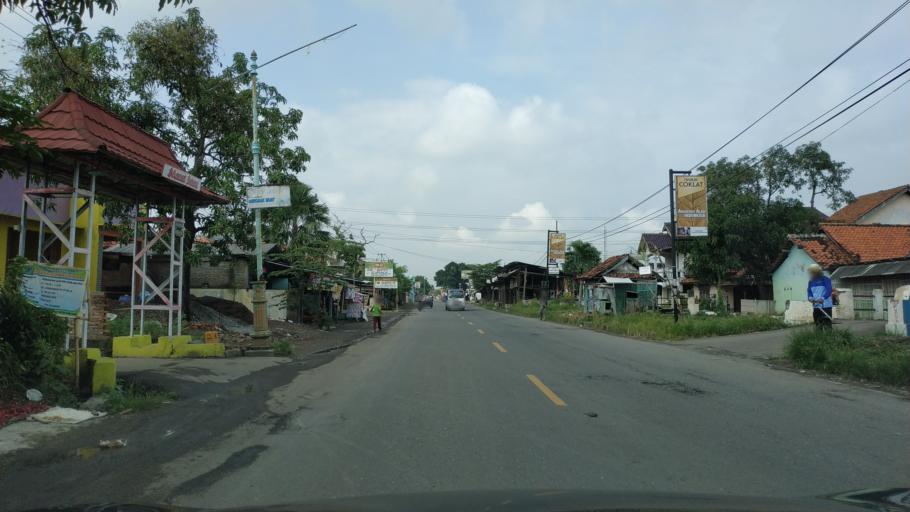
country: ID
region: Central Java
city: Ketanggungan
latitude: -6.8783
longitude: 108.8855
